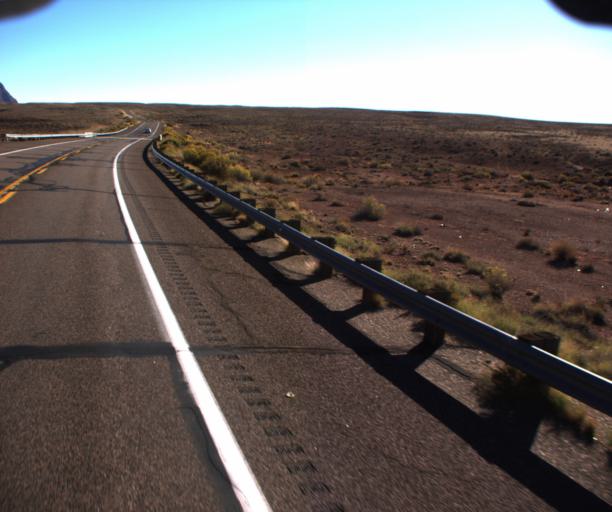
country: US
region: Arizona
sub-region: Coconino County
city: LeChee
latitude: 36.6955
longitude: -111.6545
